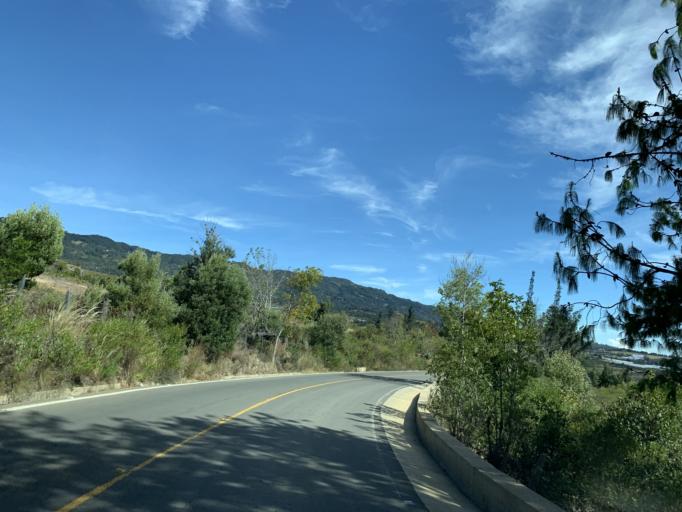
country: CO
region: Boyaca
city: Santa Sofia
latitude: 5.7035
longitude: -73.5912
